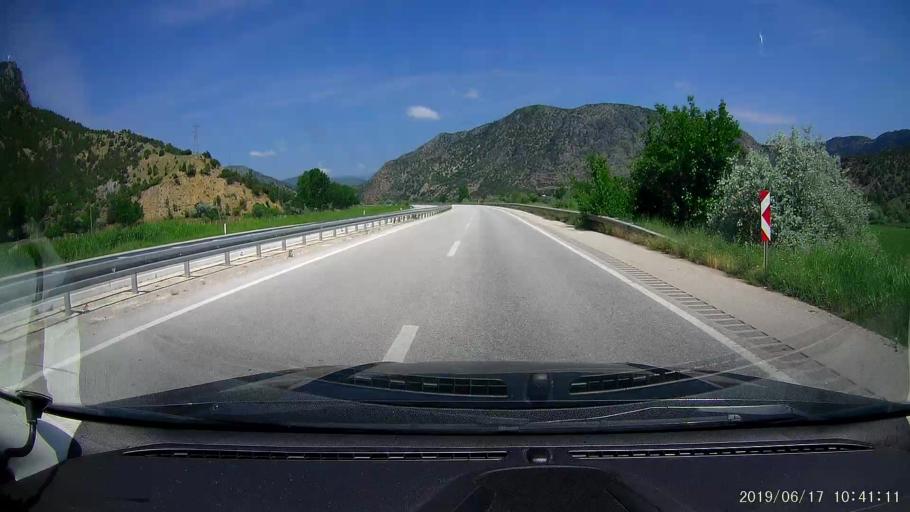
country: TR
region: Corum
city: Kargi
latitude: 41.0366
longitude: 34.5824
